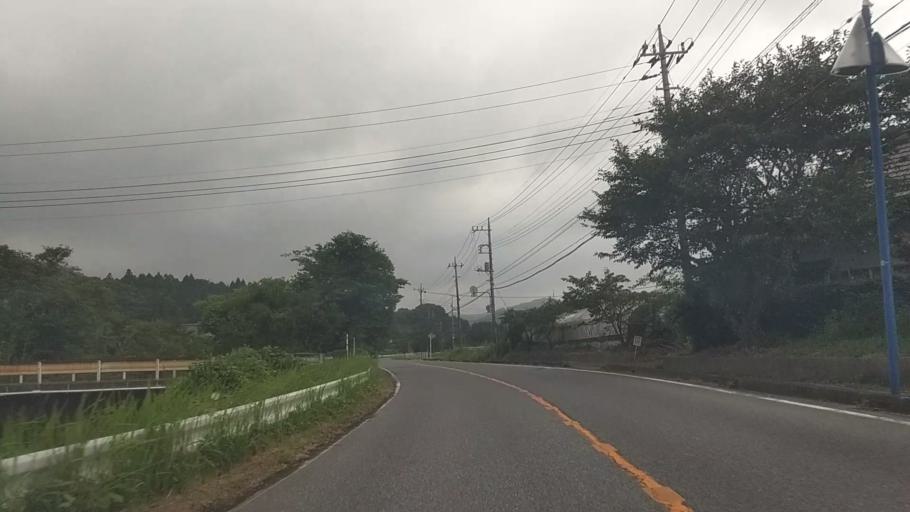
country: JP
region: Chiba
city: Kawaguchi
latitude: 35.1374
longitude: 139.9807
